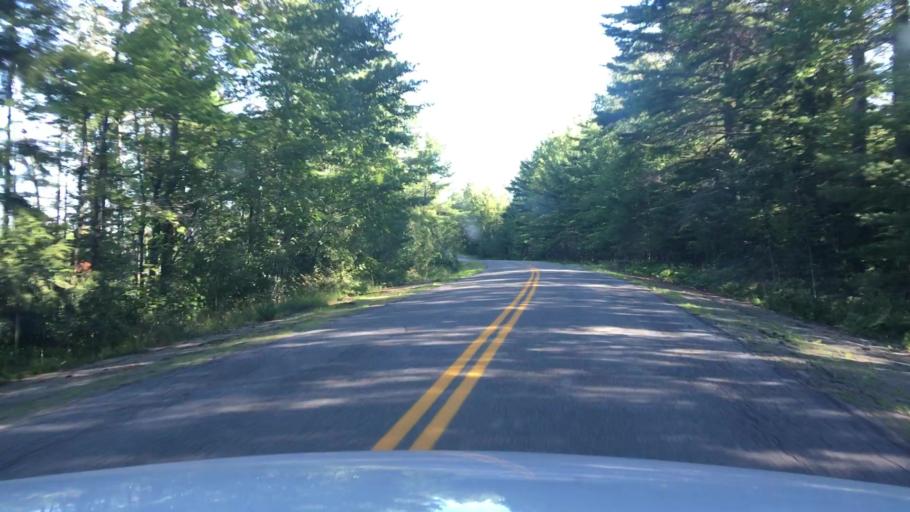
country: US
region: Maine
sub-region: Penobscot County
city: Enfield
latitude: 45.2321
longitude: -68.5806
